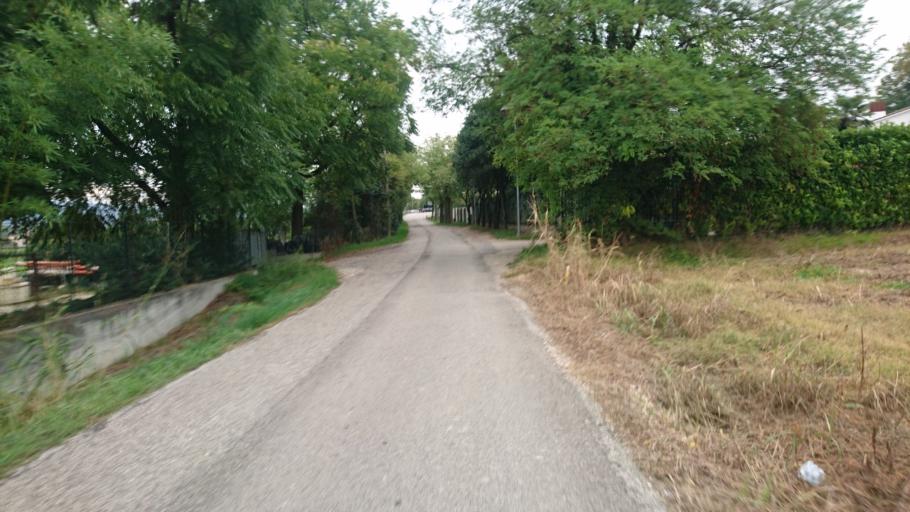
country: IT
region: Veneto
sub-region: Provincia di Verona
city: San Martino Buon Albergo
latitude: 45.4089
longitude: 11.0780
